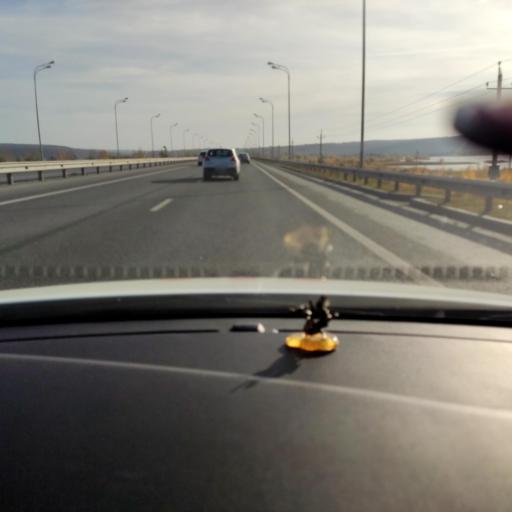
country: RU
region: Tatarstan
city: Osinovo
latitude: 55.8090
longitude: 48.8415
